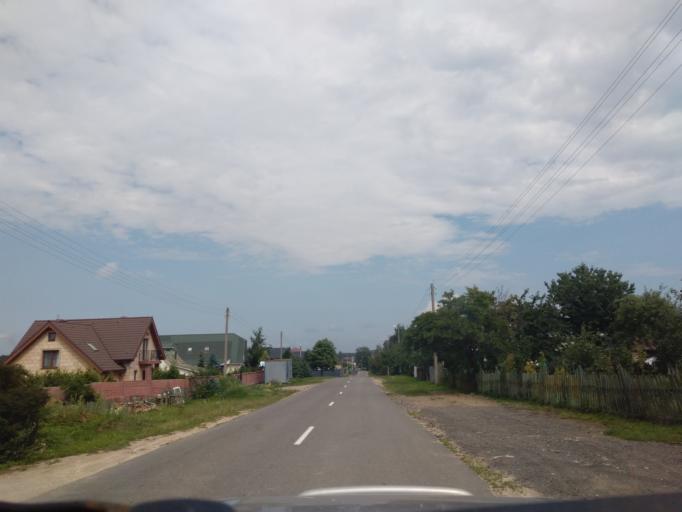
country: BY
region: Minsk
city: Khatsyezhyna
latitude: 53.9060
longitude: 27.2996
